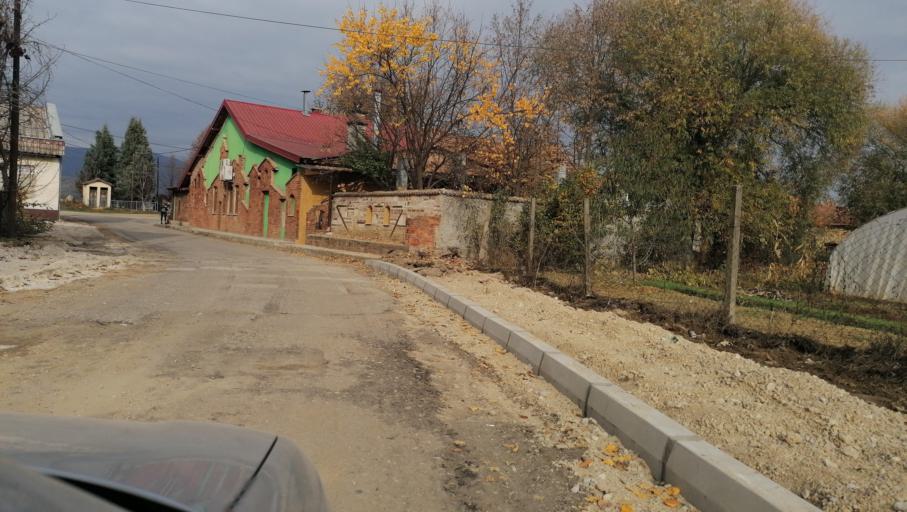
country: MK
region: Cesinovo-Oblesevo
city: Cesinovo
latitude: 41.8754
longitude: 22.2950
